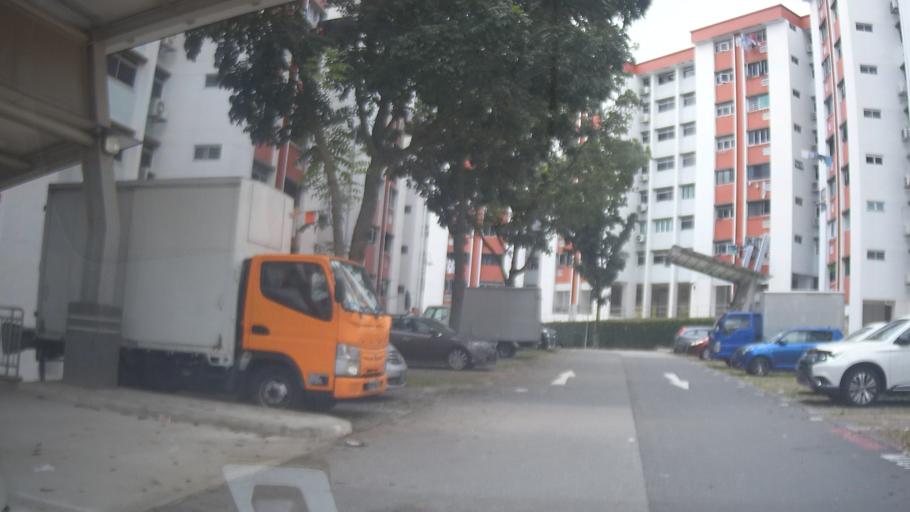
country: MY
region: Johor
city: Johor Bahru
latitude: 1.4367
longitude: 103.7770
